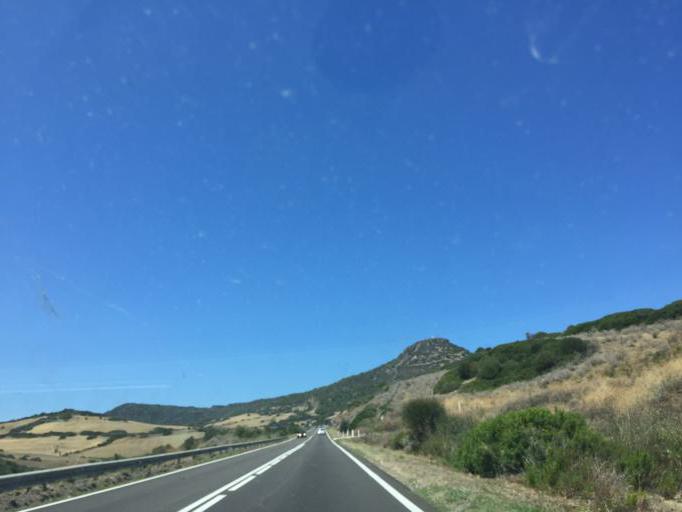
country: IT
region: Sardinia
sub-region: Provincia di Sassari
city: Valledoria
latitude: 40.9021
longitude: 8.7867
